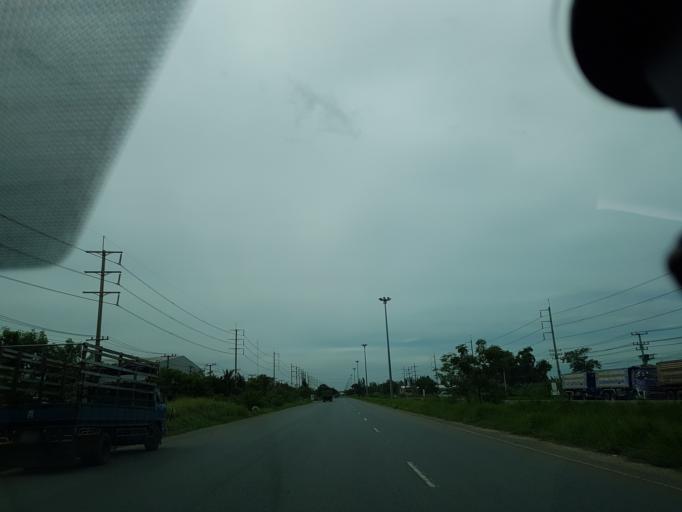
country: TH
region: Pathum Thani
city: Sam Khok
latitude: 14.1121
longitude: 100.5701
